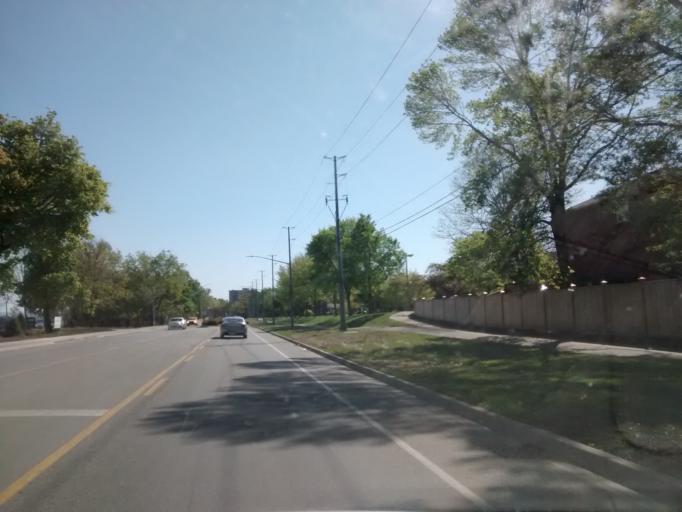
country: CA
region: Ontario
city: Oakville
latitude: 43.3742
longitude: -79.7218
